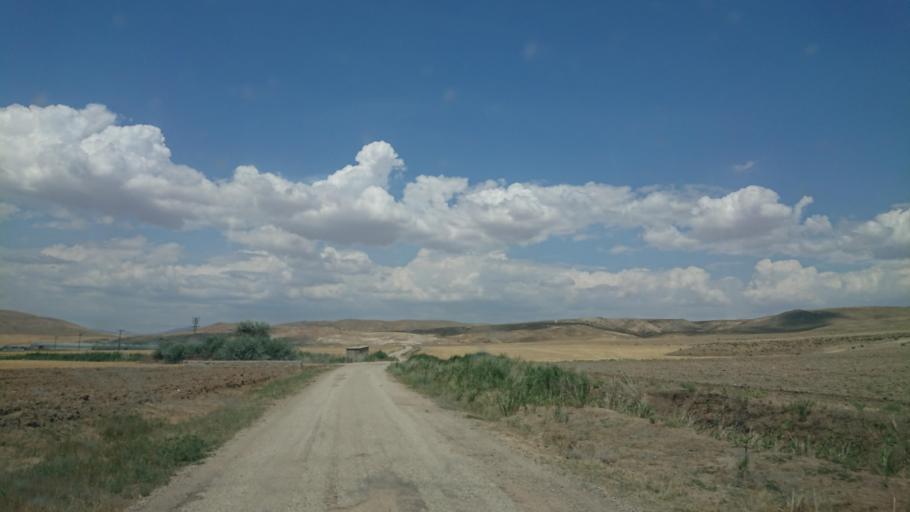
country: TR
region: Aksaray
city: Sariyahsi
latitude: 38.9902
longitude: 33.9103
